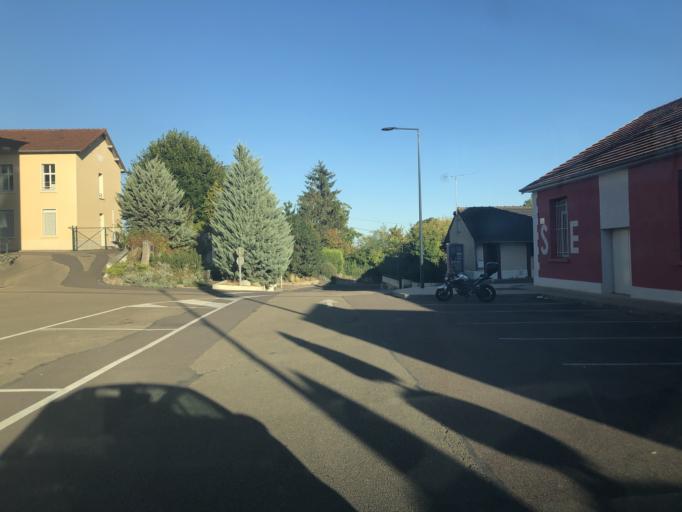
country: FR
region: Bourgogne
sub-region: Departement de l'Yonne
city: Joigny
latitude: 47.9829
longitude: 3.4070
